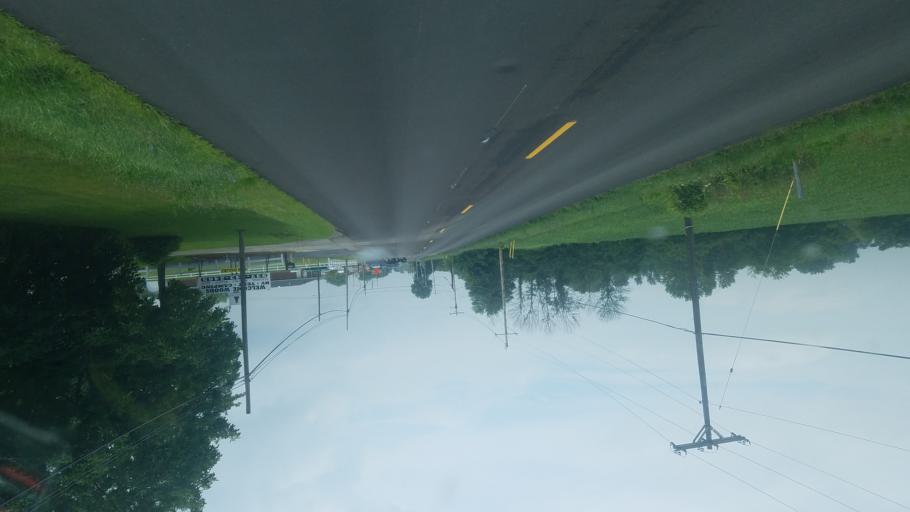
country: US
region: Ohio
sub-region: Logan County
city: Russells Point
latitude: 40.4696
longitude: -83.8602
